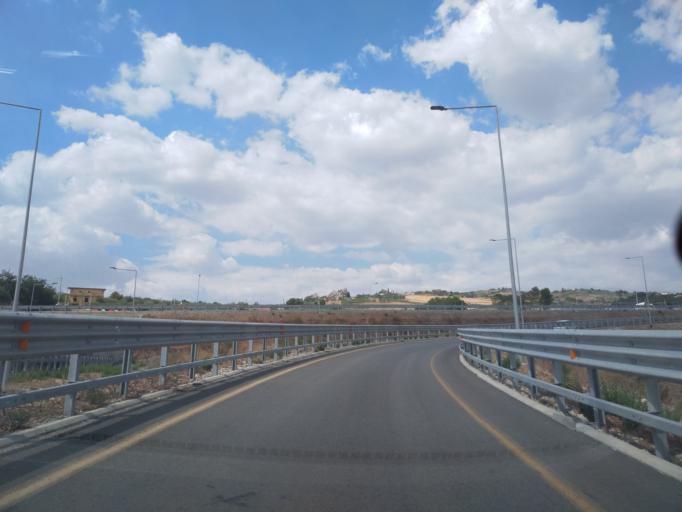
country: IT
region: Sicily
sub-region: Provincia di Caltanissetta
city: San Cataldo
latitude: 37.4496
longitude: 13.9703
